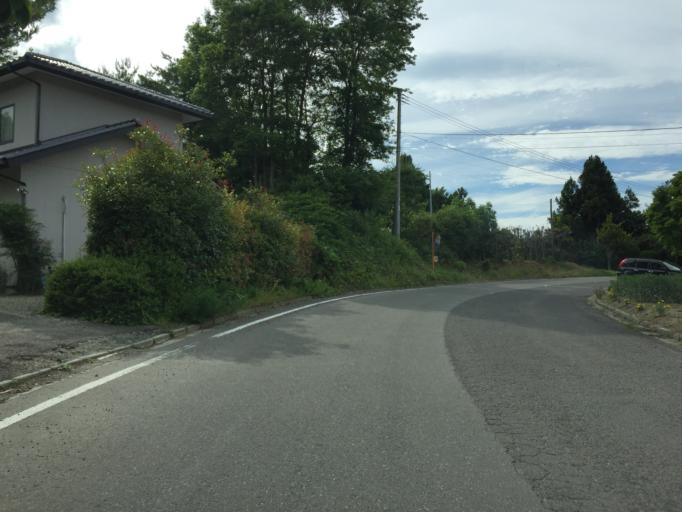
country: JP
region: Fukushima
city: Funehikimachi-funehiki
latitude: 37.5268
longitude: 140.5597
